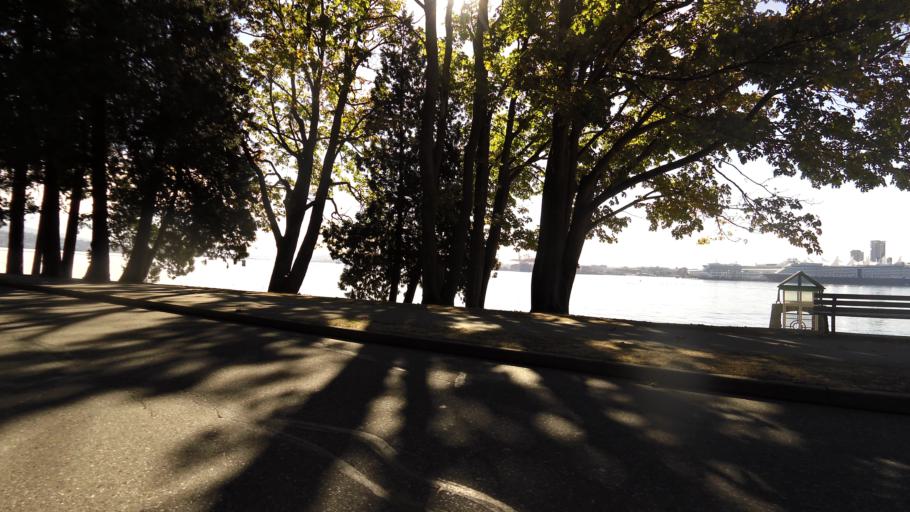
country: CA
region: British Columbia
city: West End
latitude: 49.2983
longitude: -123.1178
